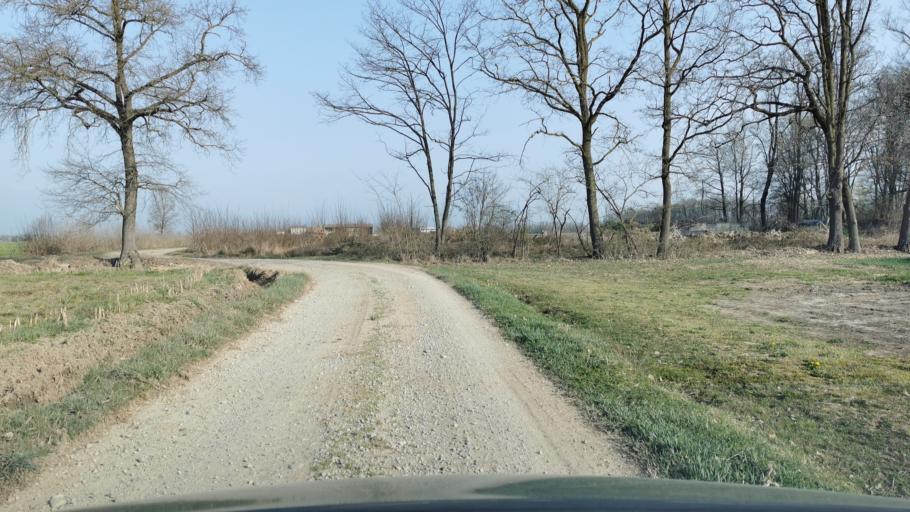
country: IT
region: Piedmont
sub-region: Provincia di Torino
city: Rivarossa
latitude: 45.2624
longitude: 7.7309
